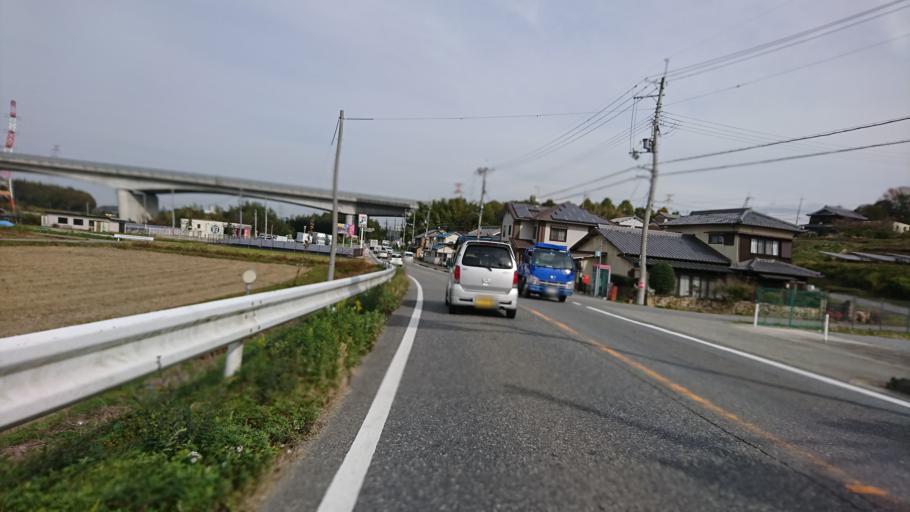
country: JP
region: Hyogo
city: Ono
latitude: 34.8094
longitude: 134.9300
